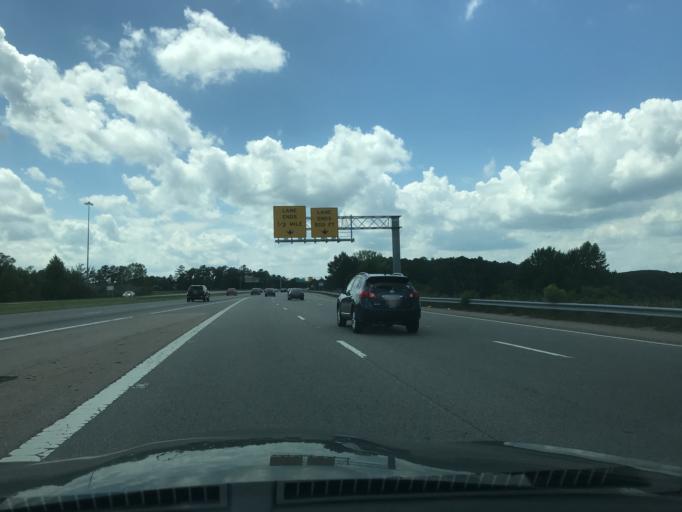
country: US
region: North Carolina
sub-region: Wake County
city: Raleigh
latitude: 35.8763
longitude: -78.5797
